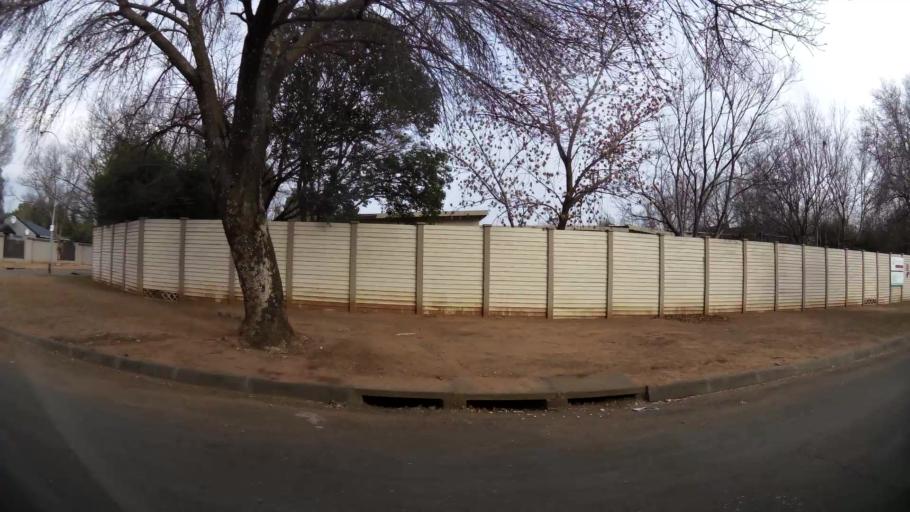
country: ZA
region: Orange Free State
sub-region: Mangaung Metropolitan Municipality
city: Bloemfontein
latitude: -29.1211
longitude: 26.1819
